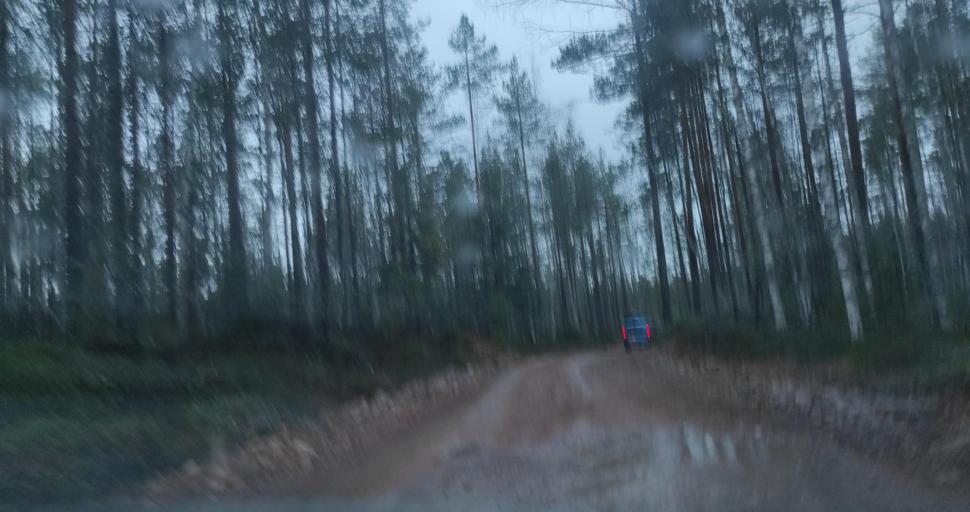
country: RU
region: Republic of Karelia
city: Salmi
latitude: 61.6280
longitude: 31.8128
